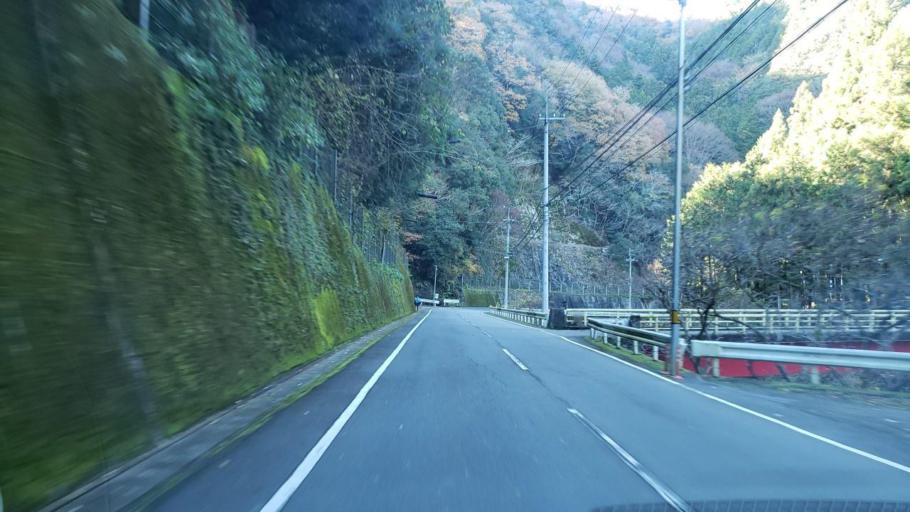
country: JP
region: Tokushima
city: Wakimachi
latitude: 34.0100
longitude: 134.0314
